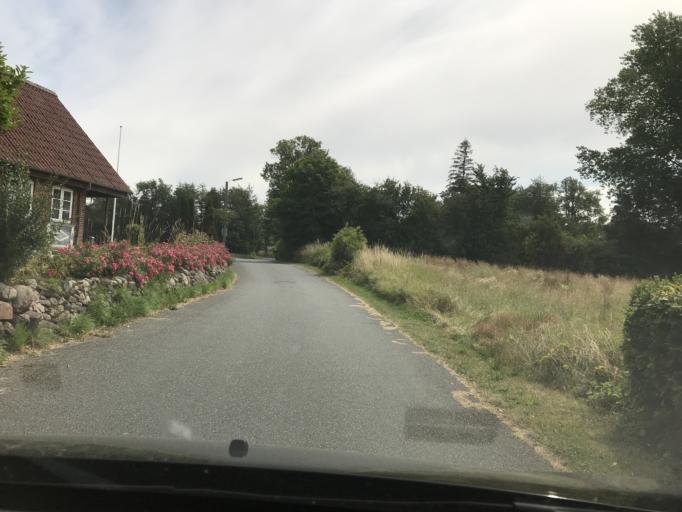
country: DK
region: South Denmark
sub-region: AEro Kommune
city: AEroskobing
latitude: 54.9125
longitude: 10.2835
